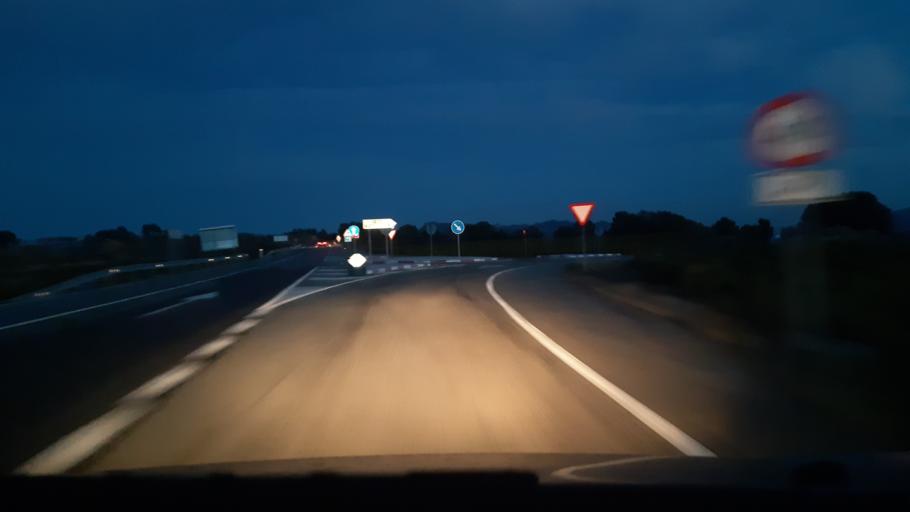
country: ES
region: Catalonia
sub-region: Provincia de Tarragona
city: Bot
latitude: 41.0491
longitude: 0.3699
